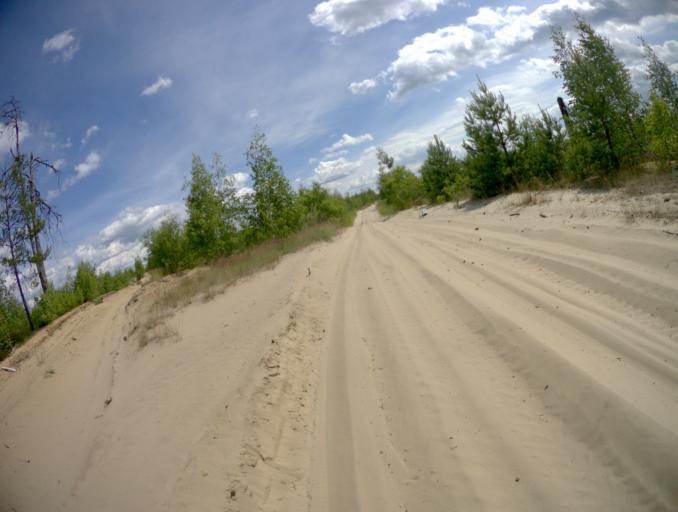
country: RU
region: Nizjnij Novgorod
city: Frolishchi
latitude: 56.4753
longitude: 42.5990
